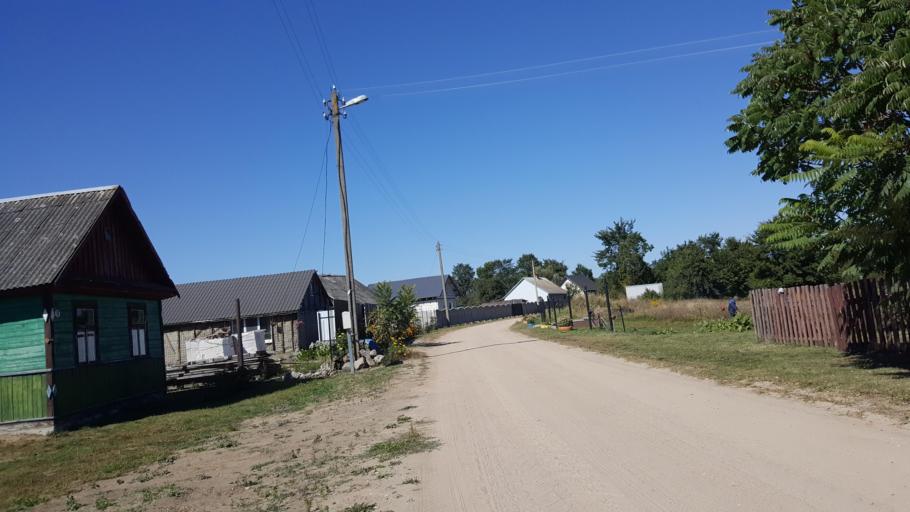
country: PL
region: Lublin Voivodeship
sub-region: Powiat bialski
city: Rokitno
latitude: 52.2189
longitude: 23.3422
